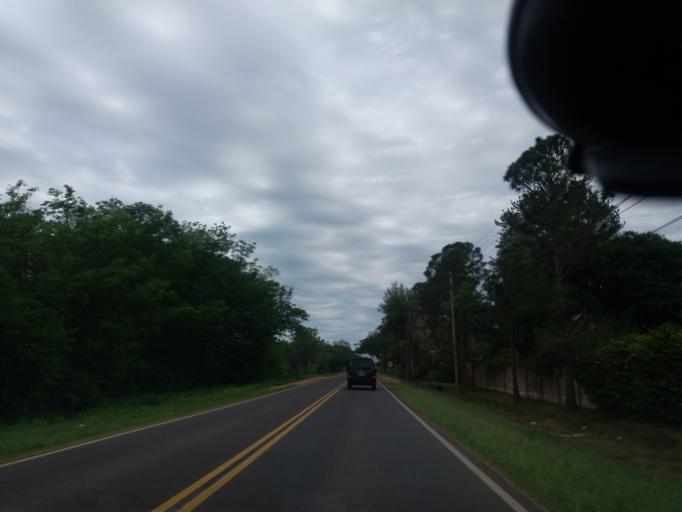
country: AR
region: Corrientes
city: Corrientes
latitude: -27.4521
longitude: -58.7271
